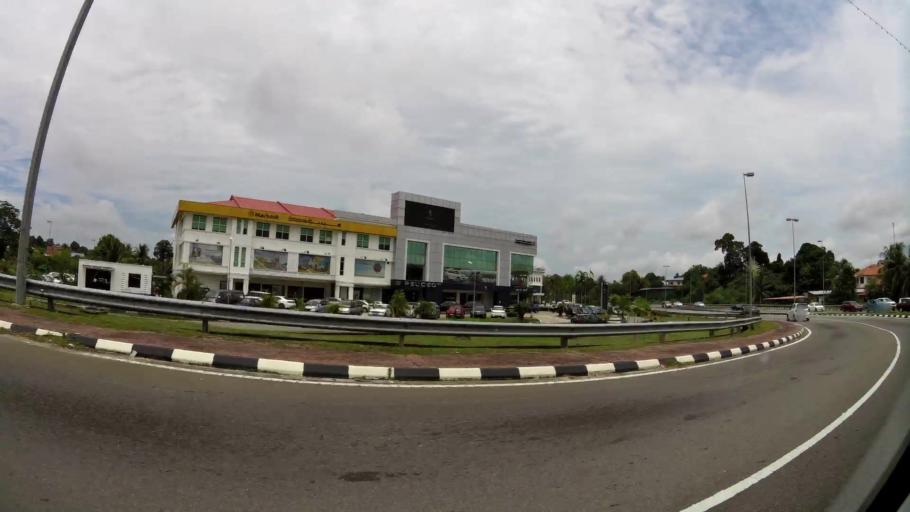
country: BN
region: Brunei and Muara
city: Bandar Seri Begawan
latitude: 4.9003
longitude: 114.9191
